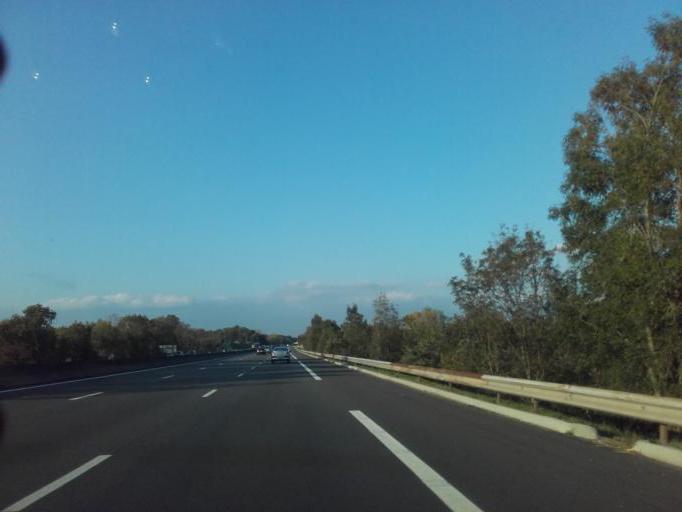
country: FR
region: Bourgogne
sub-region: Departement de Saone-et-Loire
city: Saint-Martin-Belle-Roche
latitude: 46.4357
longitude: 4.8699
